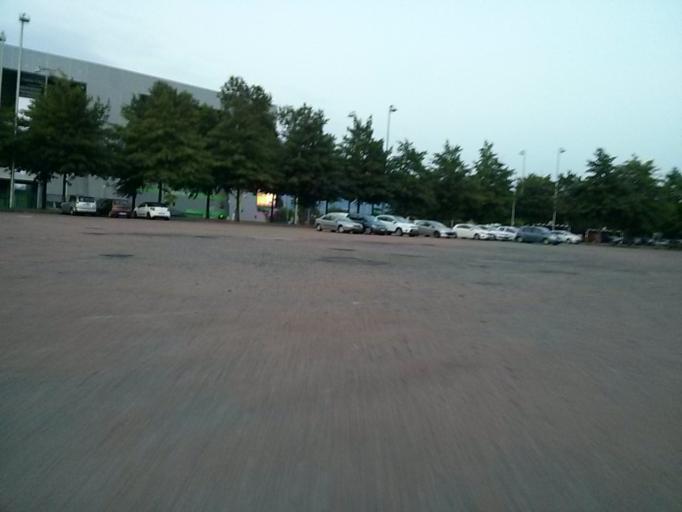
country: FR
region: Rhone-Alpes
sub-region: Departement de la Loire
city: Saint-Priest-en-Jarez
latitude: 45.4607
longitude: 4.3876
